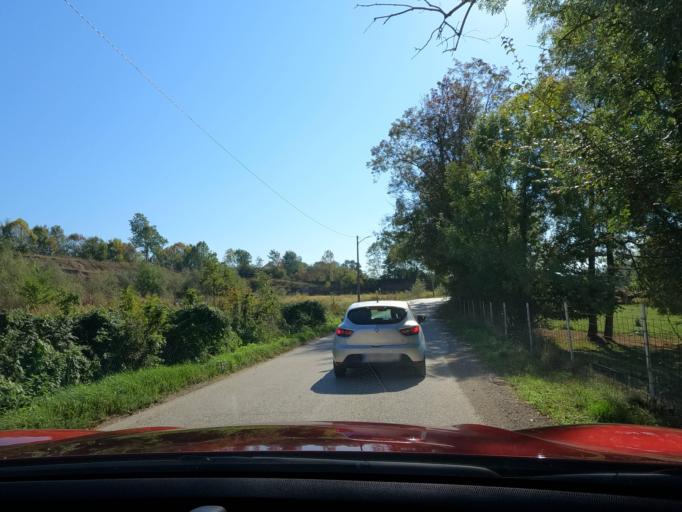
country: RS
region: Central Serbia
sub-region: Raski Okrug
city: Kraljevo
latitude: 43.7674
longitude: 20.6671
